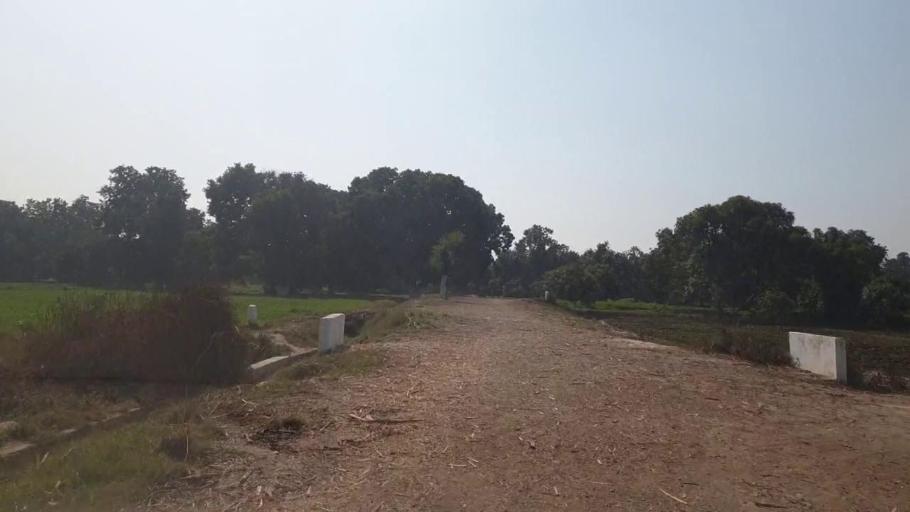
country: PK
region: Sindh
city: Tando Adam
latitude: 25.6228
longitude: 68.7353
